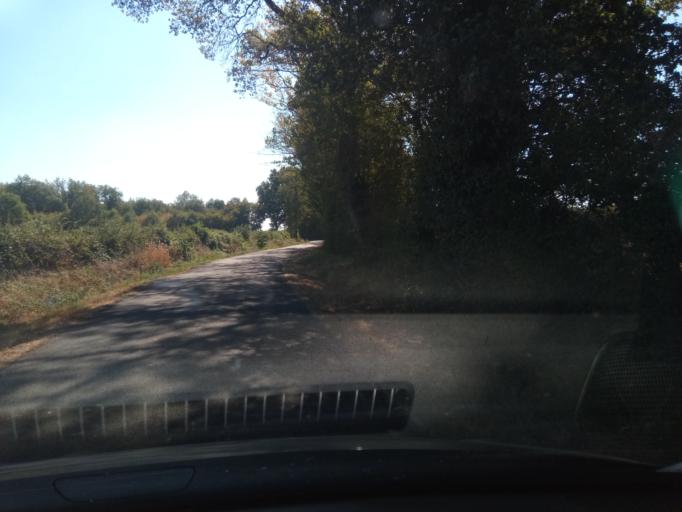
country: FR
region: Poitou-Charentes
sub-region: Departement de la Vienne
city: Lussac-les-Chateaux
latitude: 46.3931
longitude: 0.7590
